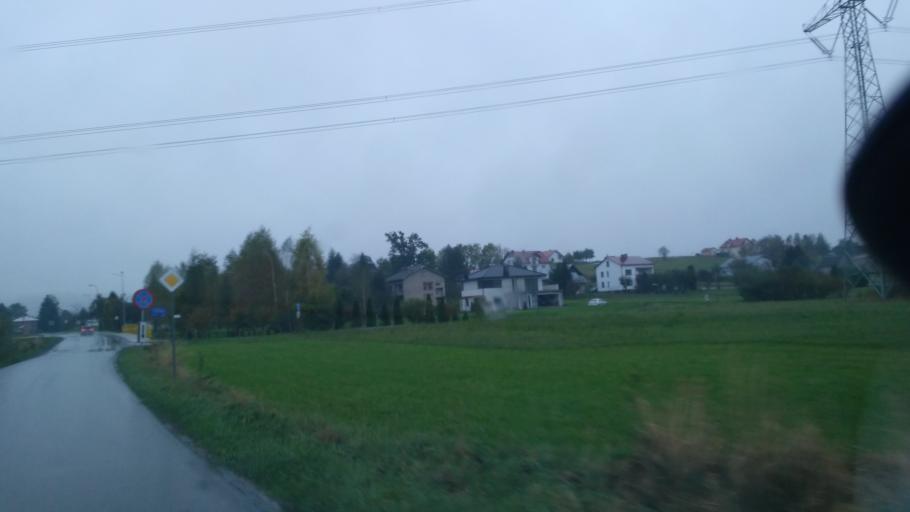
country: PL
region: Subcarpathian Voivodeship
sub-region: Powiat krosnienski
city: Korczyna
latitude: 49.6982
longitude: 21.8105
